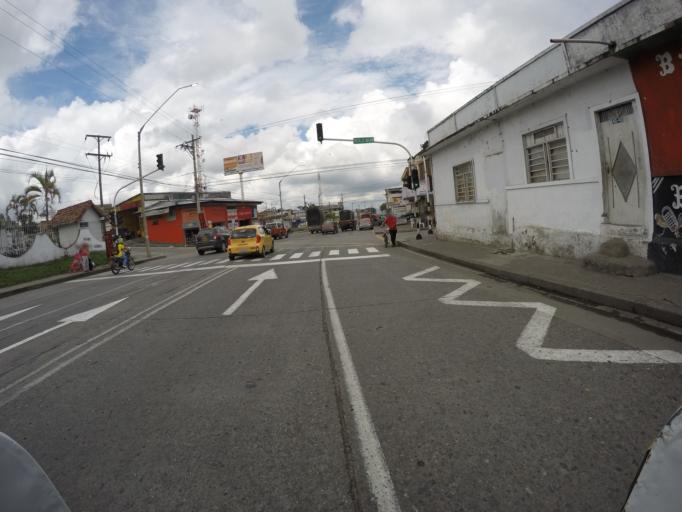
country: CO
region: Quindio
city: Armenia
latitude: 4.5230
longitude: -75.6856
